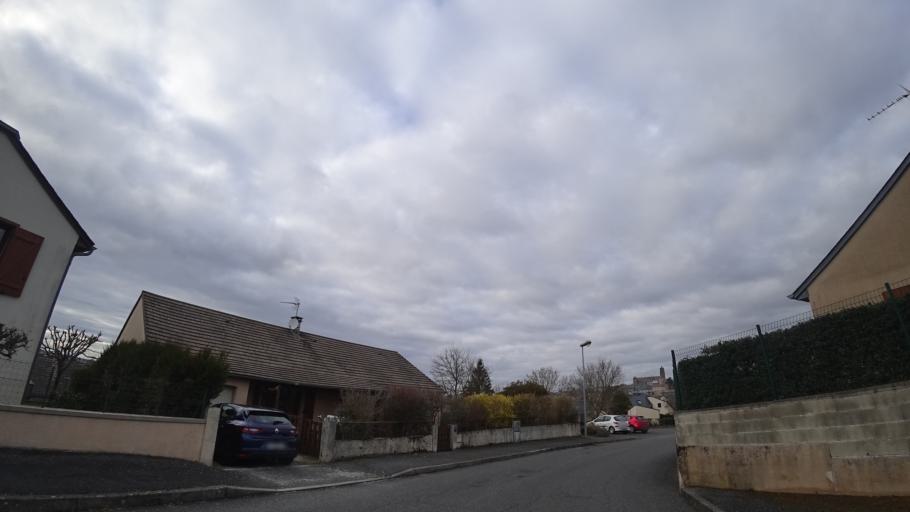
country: FR
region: Midi-Pyrenees
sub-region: Departement de l'Aveyron
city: Le Monastere
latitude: 44.3393
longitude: 2.5710
